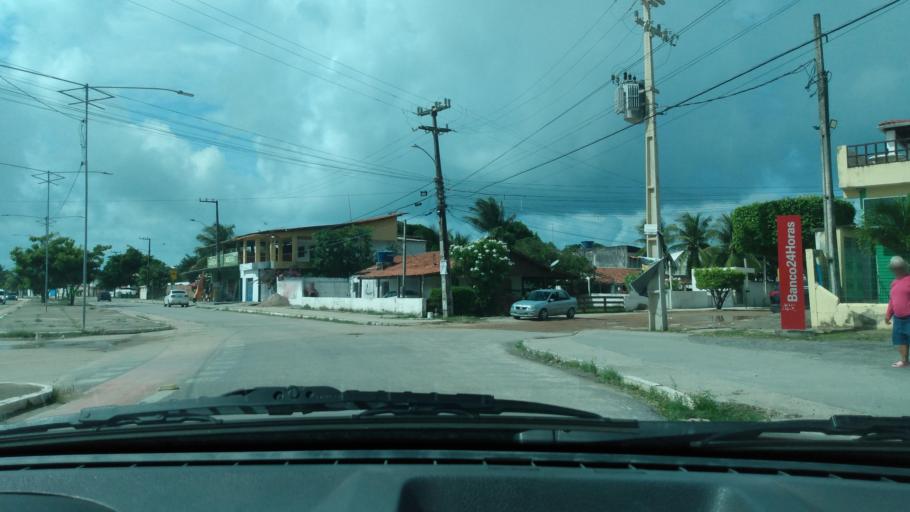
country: BR
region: Pernambuco
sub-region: Cabo De Santo Agostinho
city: Cabo
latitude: -8.3211
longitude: -34.9526
